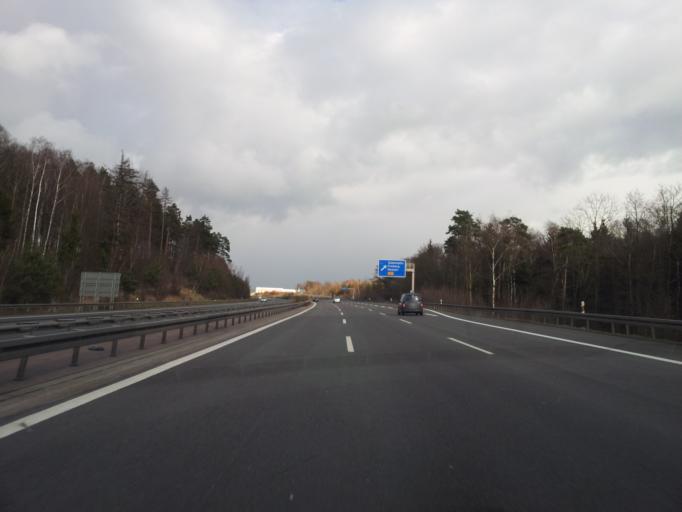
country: DE
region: Saxony
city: Nossen
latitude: 51.0337
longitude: 13.2833
